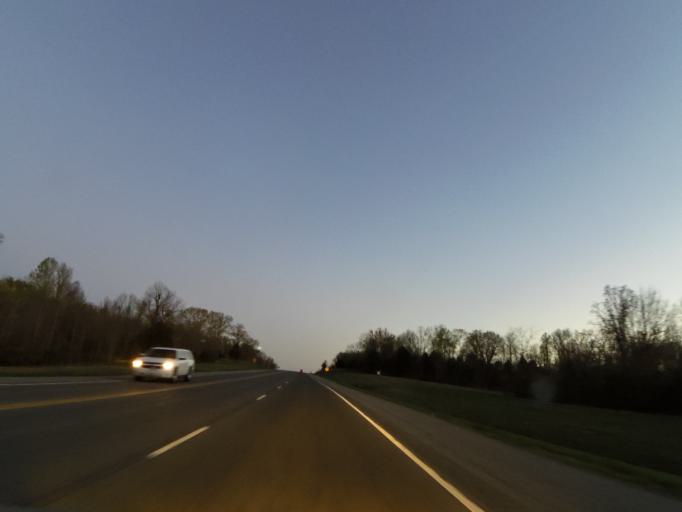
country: US
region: Tennessee
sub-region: Robertson County
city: Springfield
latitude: 36.4541
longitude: -86.8986
